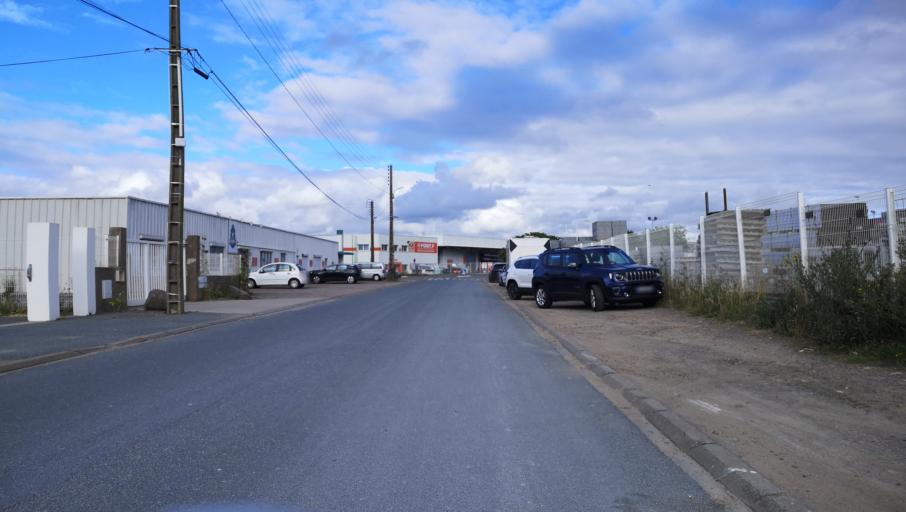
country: FR
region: Pays de la Loire
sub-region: Departement de la Vendee
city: Les Sables-d'Olonne
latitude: 46.5168
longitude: -1.7825
